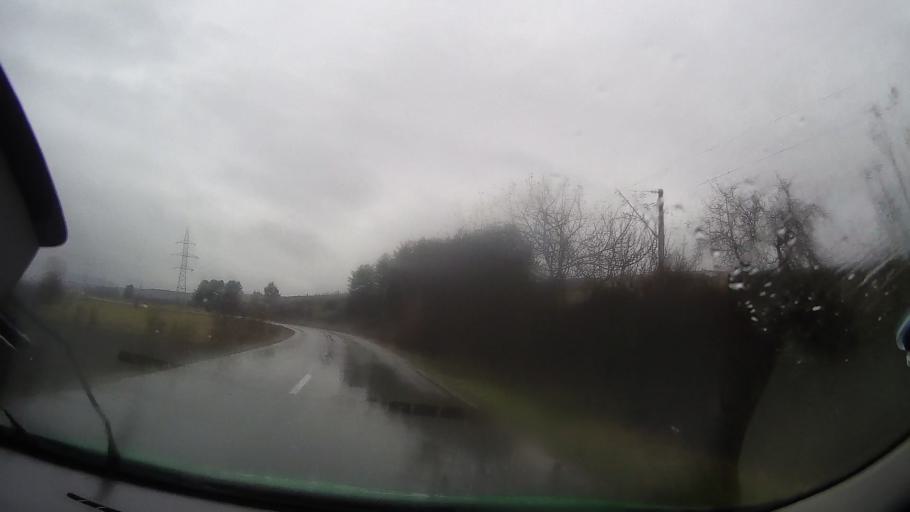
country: RO
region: Bistrita-Nasaud
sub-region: Comuna Mariselu
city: Mariselu
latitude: 47.0273
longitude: 24.4949
